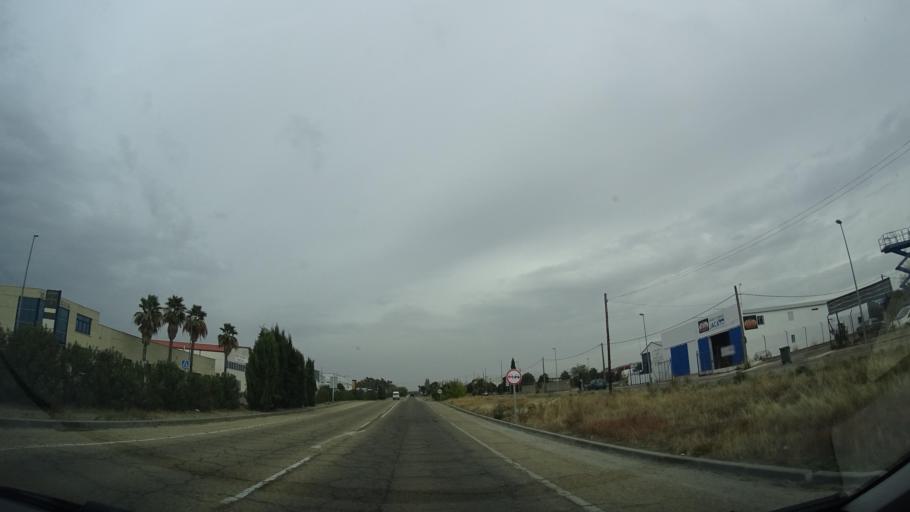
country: ES
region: Extremadura
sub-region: Provincia de Caceres
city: Trujillo
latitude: 39.4758
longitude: -5.8580
